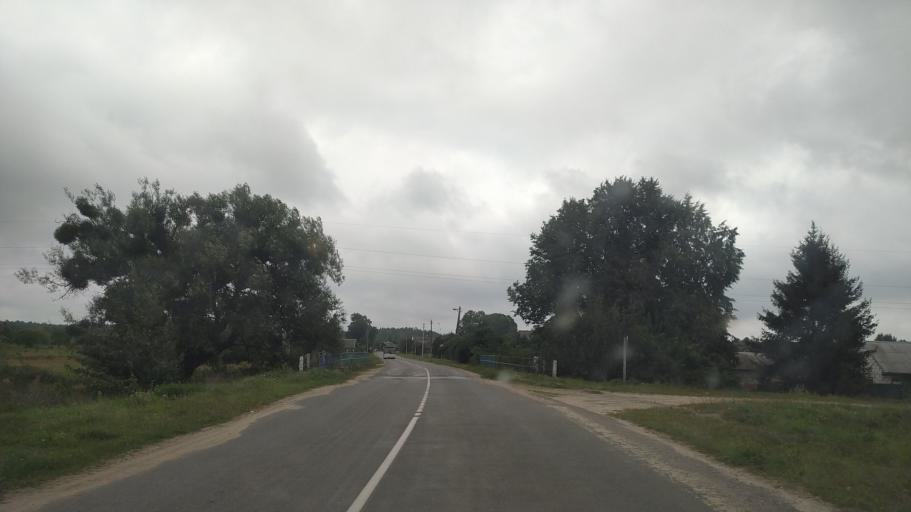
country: BY
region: Brest
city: Byaroza
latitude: 52.5925
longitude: 24.8710
